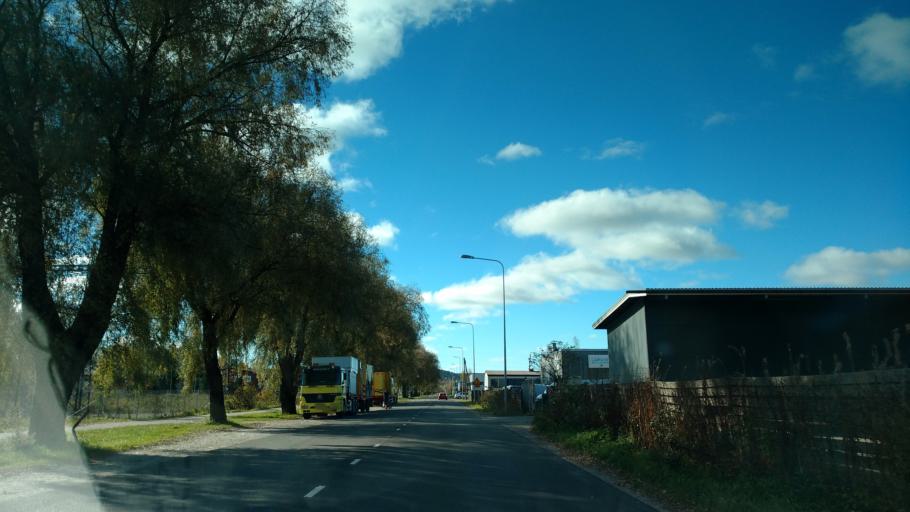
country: FI
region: Varsinais-Suomi
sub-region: Salo
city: Salo
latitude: 60.3774
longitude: 23.1121
